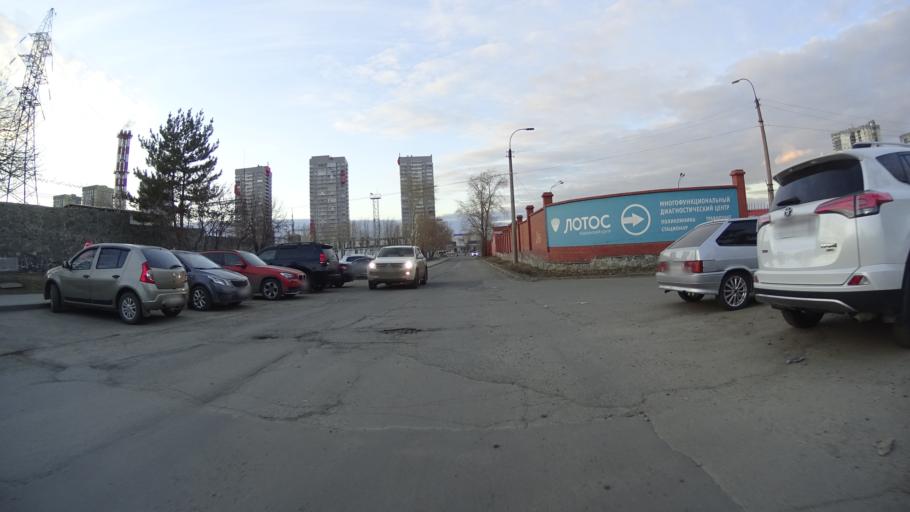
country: RU
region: Chelyabinsk
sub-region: Gorod Chelyabinsk
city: Chelyabinsk
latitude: 55.1688
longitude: 61.3702
